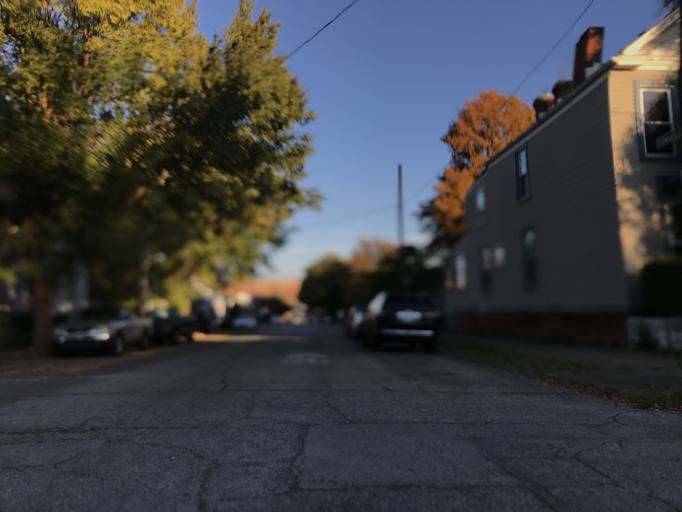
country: US
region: Kentucky
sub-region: Jefferson County
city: Louisville
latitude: 38.2404
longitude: -85.7290
